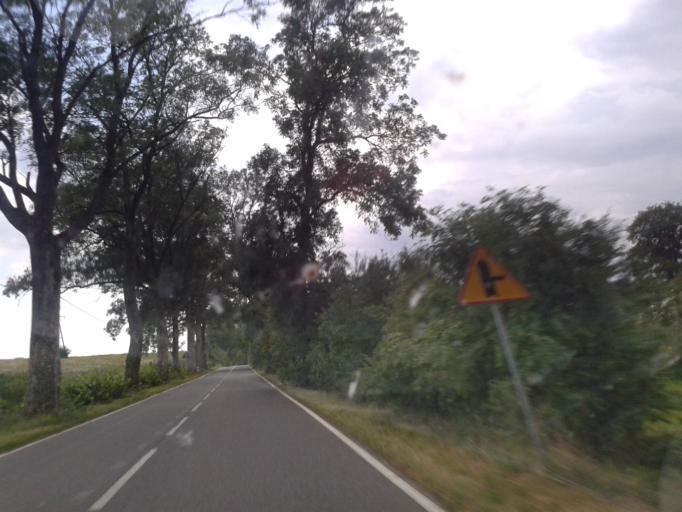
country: PL
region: West Pomeranian Voivodeship
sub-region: Powiat szczecinecki
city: Grzmiaca
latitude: 53.8767
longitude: 16.4951
